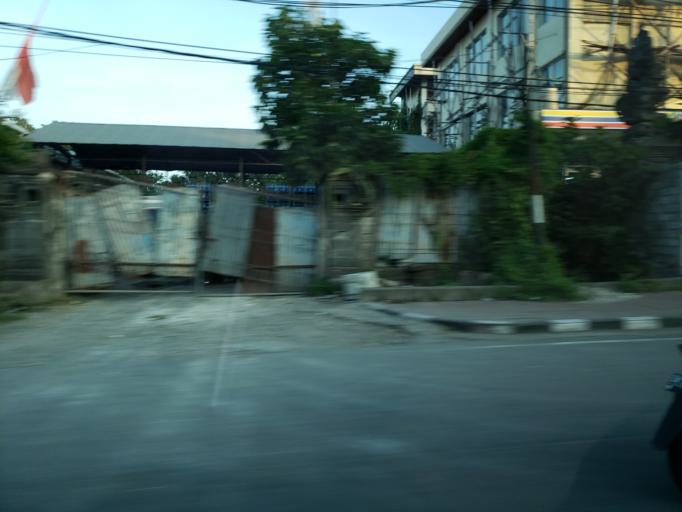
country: ID
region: Bali
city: Jimbaran
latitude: -8.7868
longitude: 115.1779
